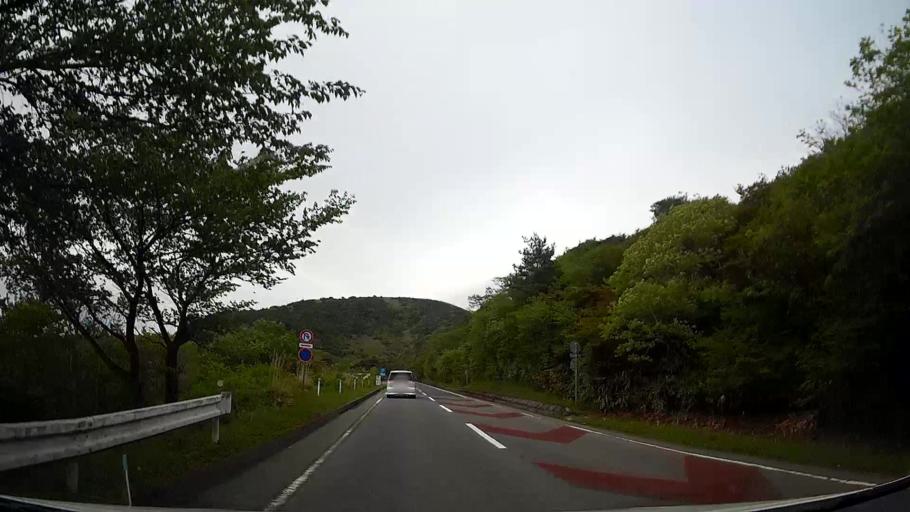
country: JP
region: Shizuoka
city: Atami
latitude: 35.0773
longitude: 139.0266
